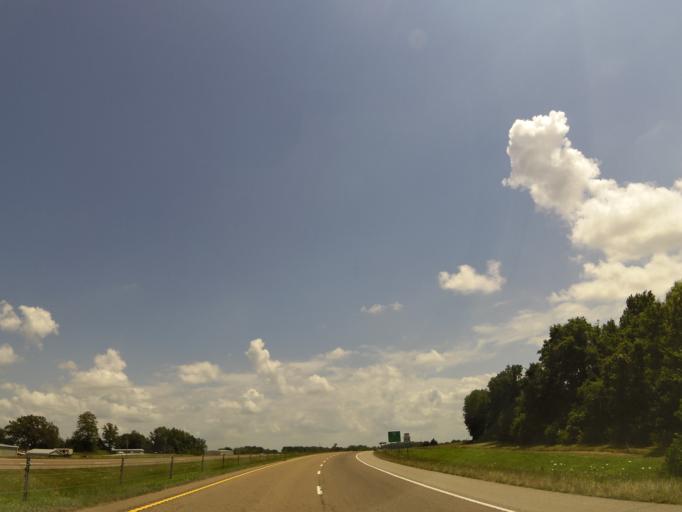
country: US
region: Tennessee
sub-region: Crockett County
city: Alamo
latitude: 35.8118
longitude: -89.1609
